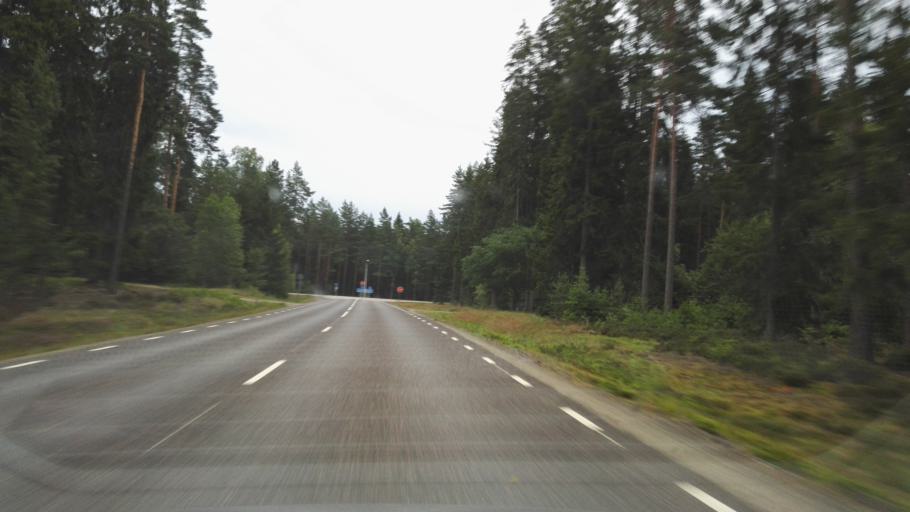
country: SE
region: Kronoberg
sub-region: Vaxjo Kommun
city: Braas
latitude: 57.0543
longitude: 15.0570
